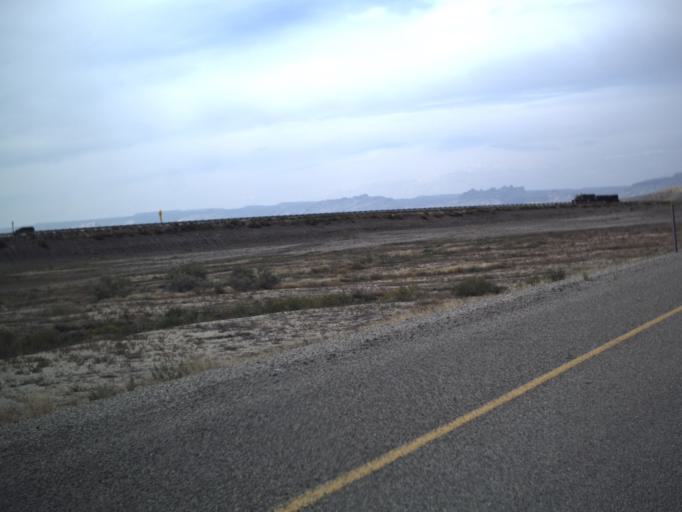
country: US
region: Utah
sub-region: Carbon County
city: East Carbon City
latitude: 38.9832
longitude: -110.2303
